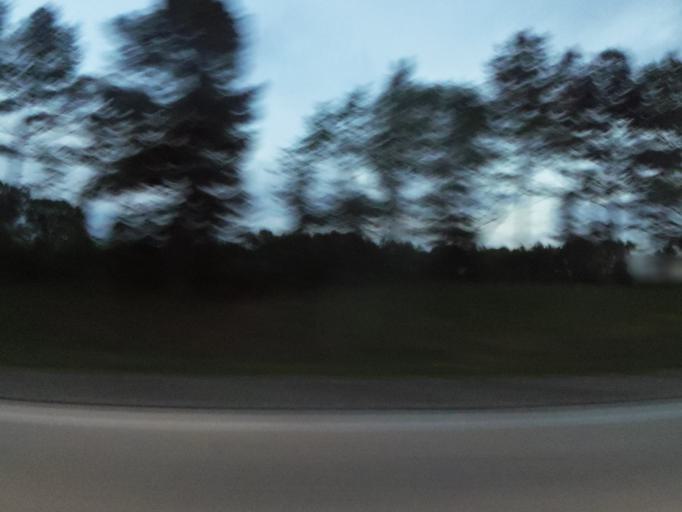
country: US
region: Georgia
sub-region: McDuffie County
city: Thomson
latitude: 33.5126
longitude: -82.4907
